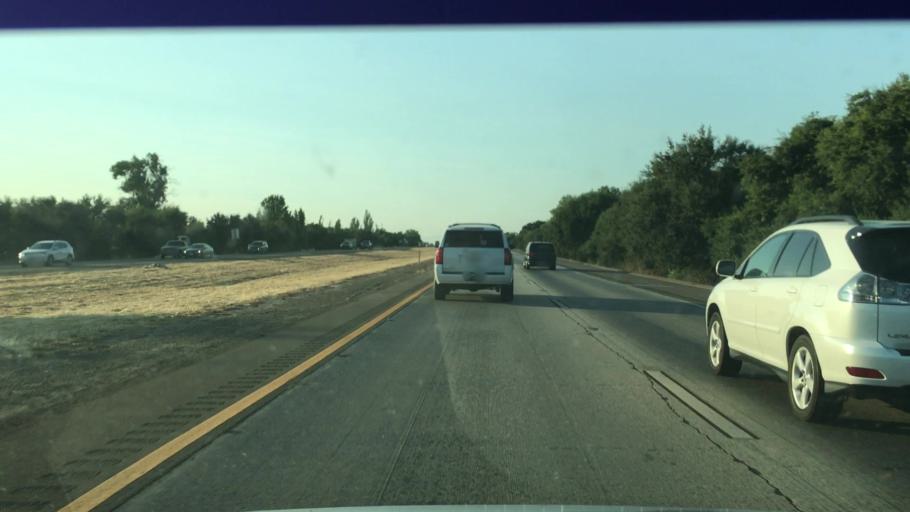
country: US
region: California
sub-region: San Joaquin County
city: Thornton
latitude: 38.2499
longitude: -121.4458
